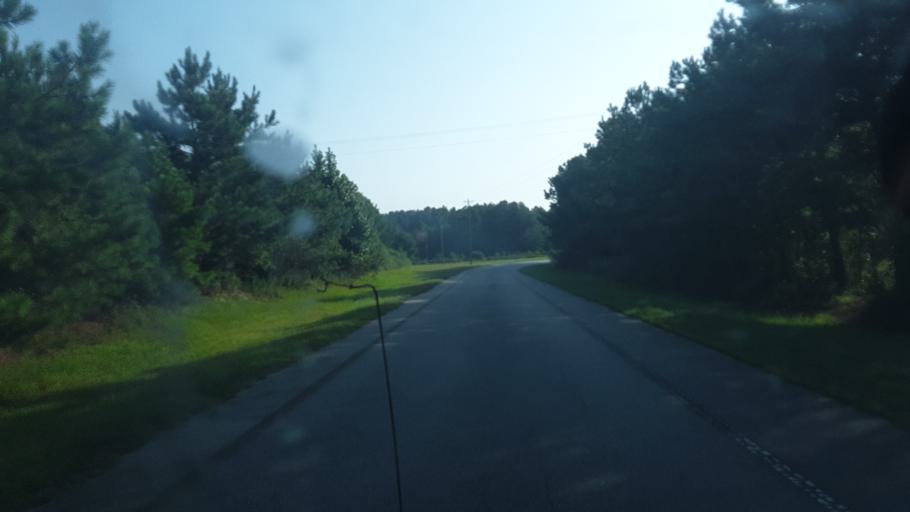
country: US
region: South Carolina
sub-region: Horry County
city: North Myrtle Beach
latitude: 33.8740
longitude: -78.6836
